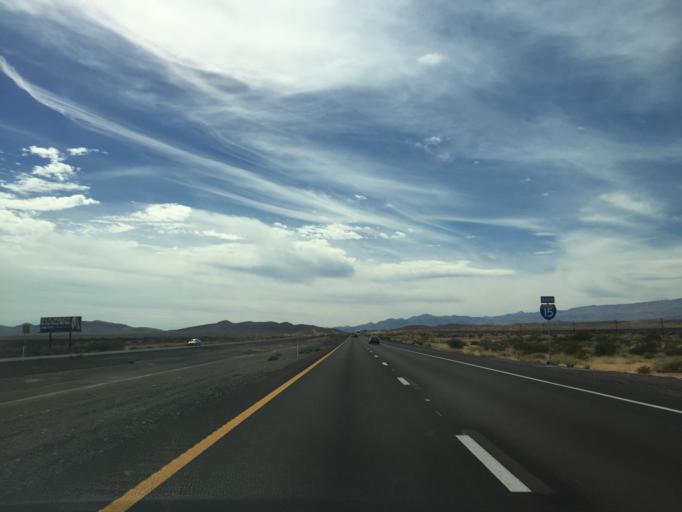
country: US
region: Nevada
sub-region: Clark County
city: Moapa Town
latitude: 36.4997
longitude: -114.7669
